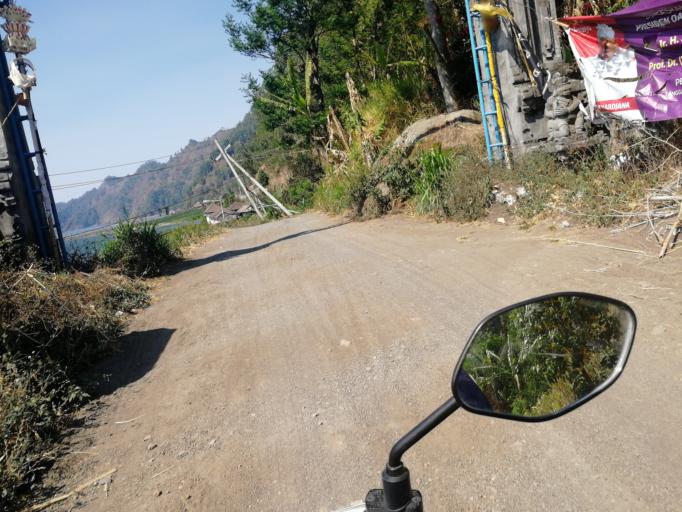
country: ID
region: Bali
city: Banjar Trunyan
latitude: -8.2701
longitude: 115.4178
